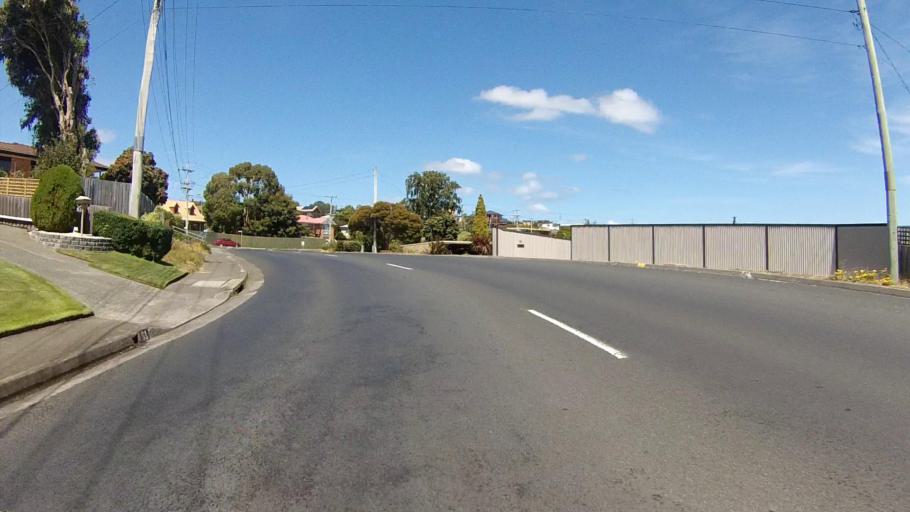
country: AU
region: Tasmania
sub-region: Sorell
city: Sorell
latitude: -42.7978
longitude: 147.5274
